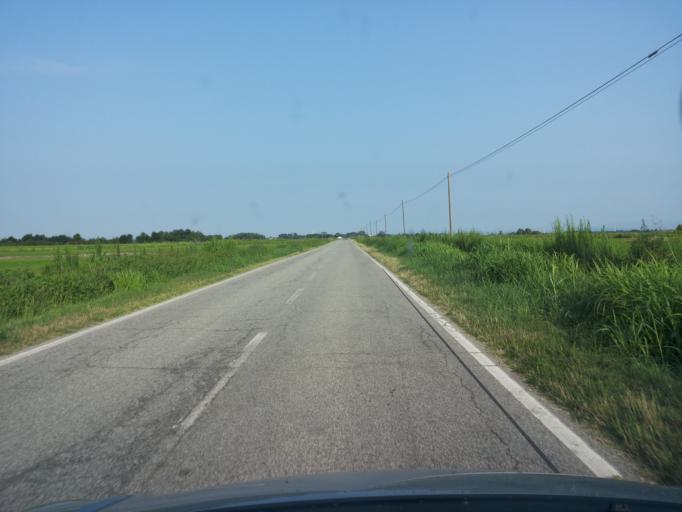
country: IT
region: Piedmont
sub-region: Provincia di Vercelli
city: Asigliano Vercellese
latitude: 45.2632
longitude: 8.3947
